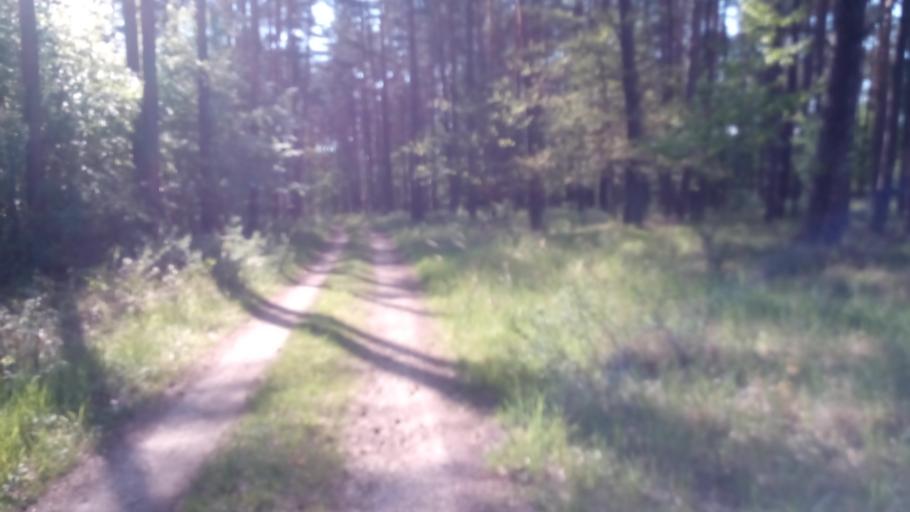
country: PL
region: Opole Voivodeship
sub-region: Powiat opolski
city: Tarnow Opolski
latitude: 50.5845
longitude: 18.0576
